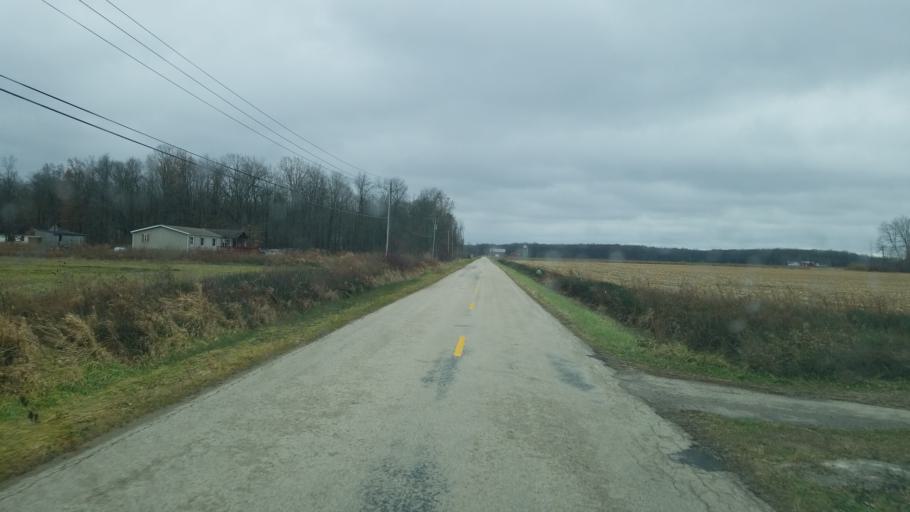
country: US
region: Ohio
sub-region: Ashtabula County
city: Roaming Shores
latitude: 41.6144
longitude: -80.8259
